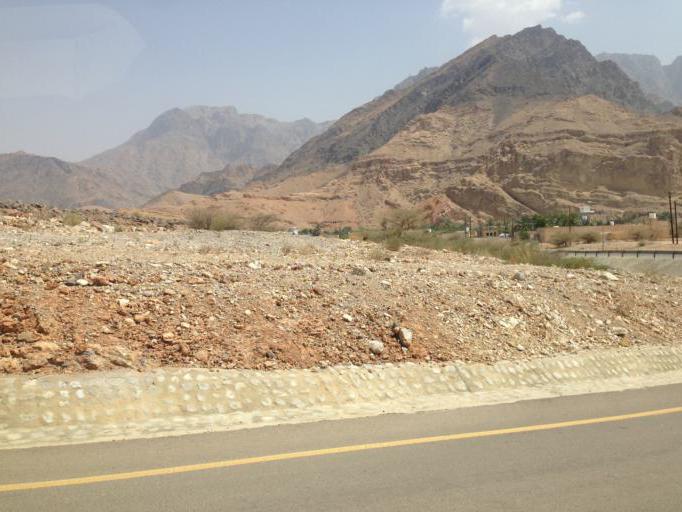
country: OM
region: Ash Sharqiyah
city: Ibra'
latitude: 23.0898
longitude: 58.8521
